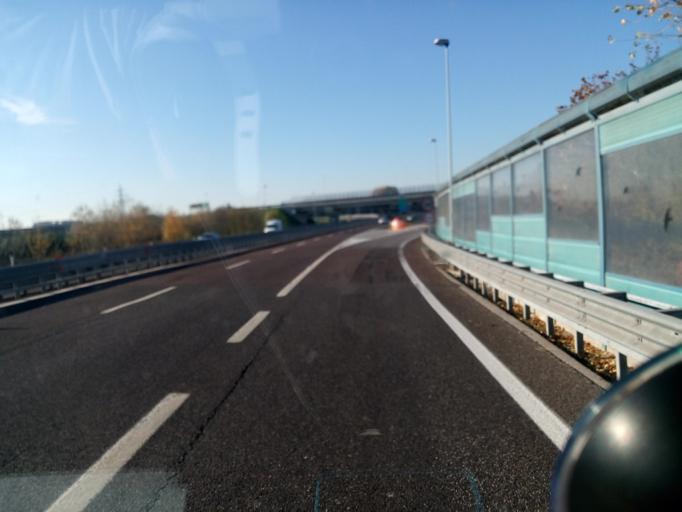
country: IT
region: Veneto
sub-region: Provincia di Padova
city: Cadoneghe
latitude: 45.4265
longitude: 11.9304
